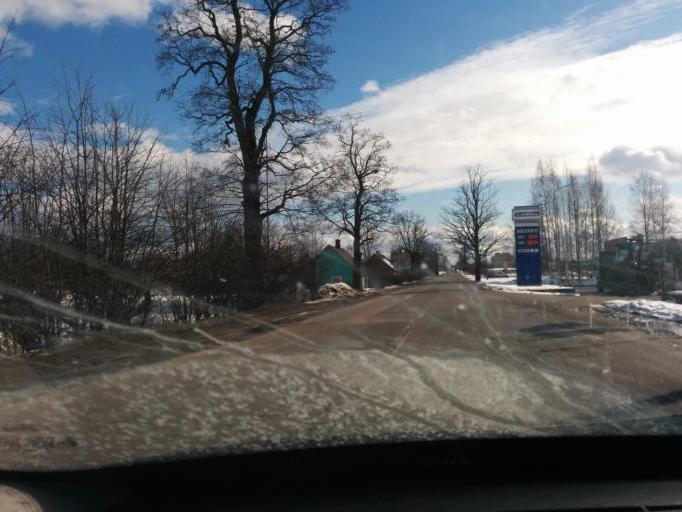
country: LV
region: Gulbenes Rajons
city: Gulbene
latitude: 57.1833
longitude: 26.7374
